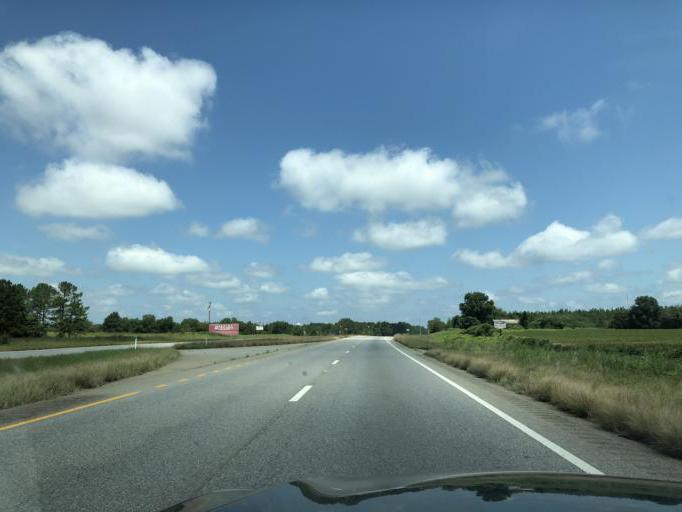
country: US
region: Alabama
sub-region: Henry County
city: Abbeville
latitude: 31.5347
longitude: -85.2906
